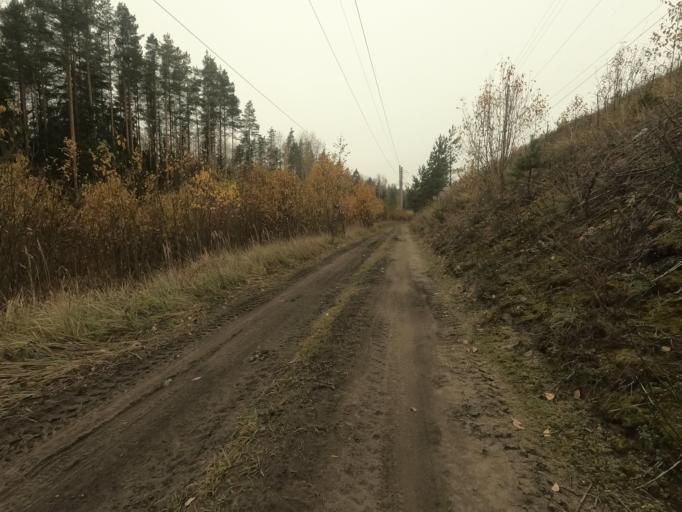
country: RU
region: Leningrad
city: Pavlovo
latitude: 59.7692
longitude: 30.9121
